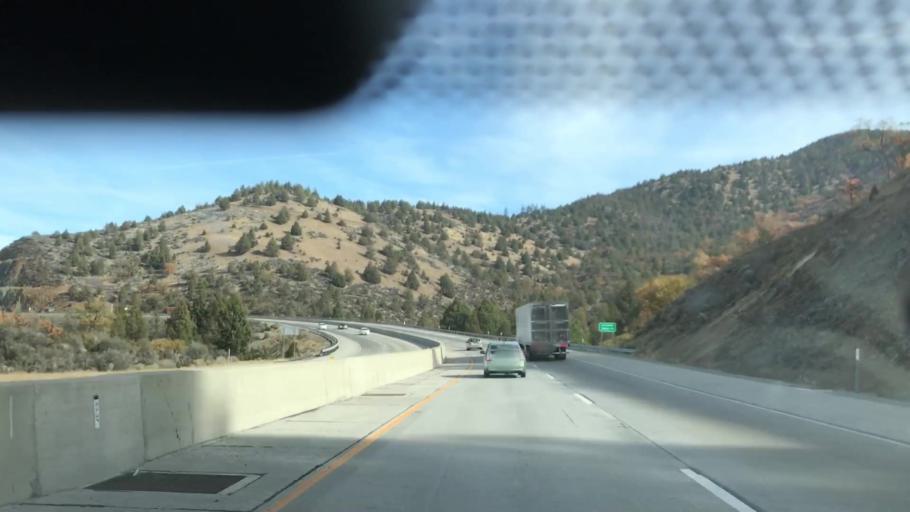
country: US
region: California
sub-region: Siskiyou County
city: Yreka
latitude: 41.7960
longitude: -122.5852
